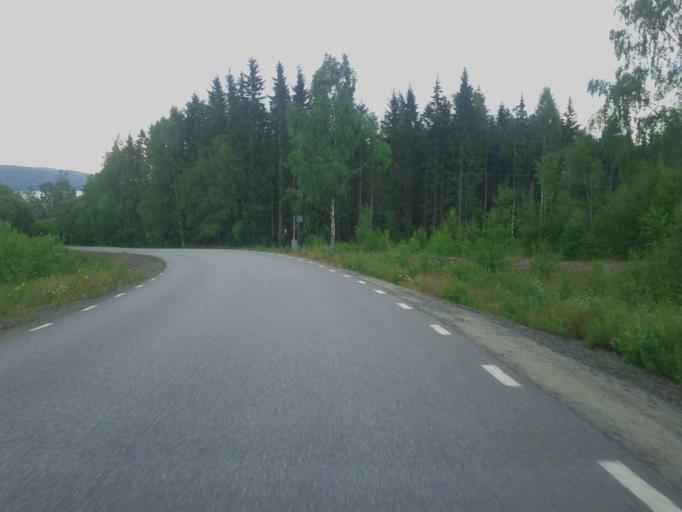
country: SE
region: Vaesternorrland
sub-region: Kramfors Kommun
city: Nordingra
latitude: 63.0655
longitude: 18.3587
